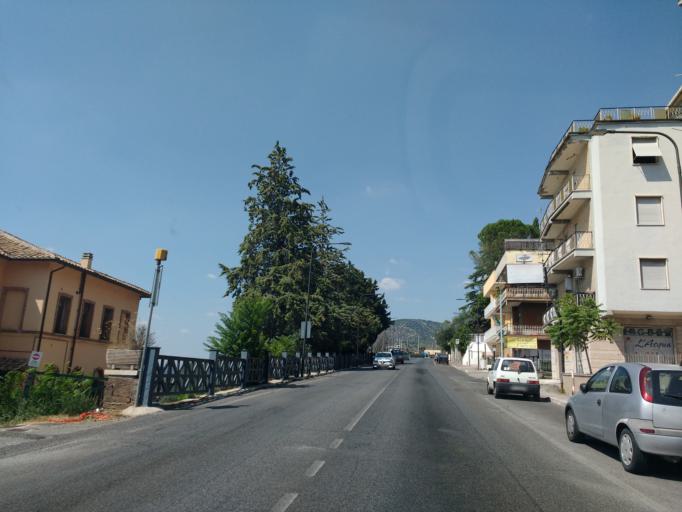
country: IT
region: Latium
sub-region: Citta metropolitana di Roma Capitale
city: Tivoli
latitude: 41.9546
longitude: 12.7918
